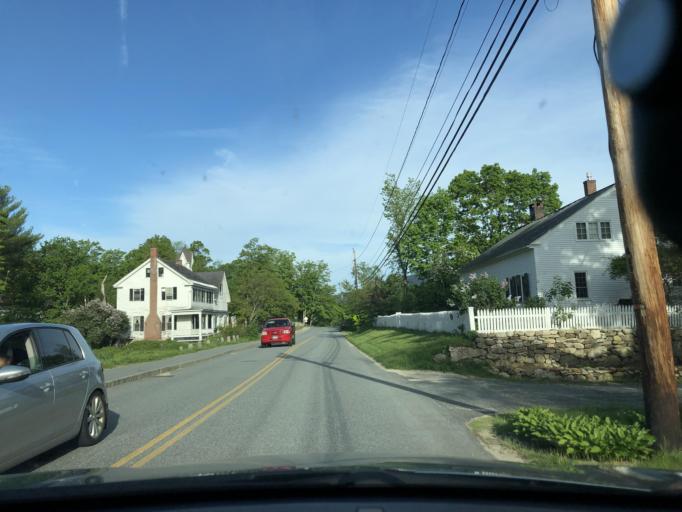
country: US
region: New Hampshire
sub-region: Merrimack County
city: Wilmot
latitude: 43.4195
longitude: -71.9367
